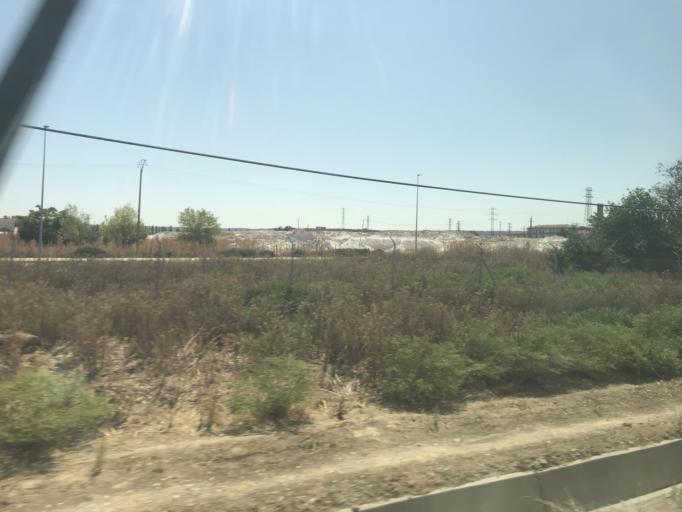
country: ES
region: Castille and Leon
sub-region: Provincia de Valladolid
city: Santovenia de Pisuerga
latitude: 41.6814
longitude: -4.6894
